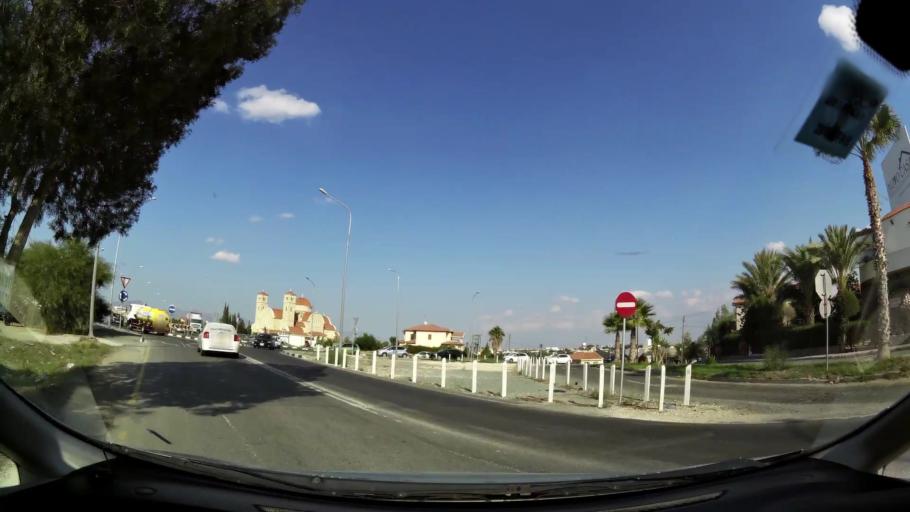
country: CY
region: Lefkosia
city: Kato Deftera
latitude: 35.1422
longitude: 33.3026
